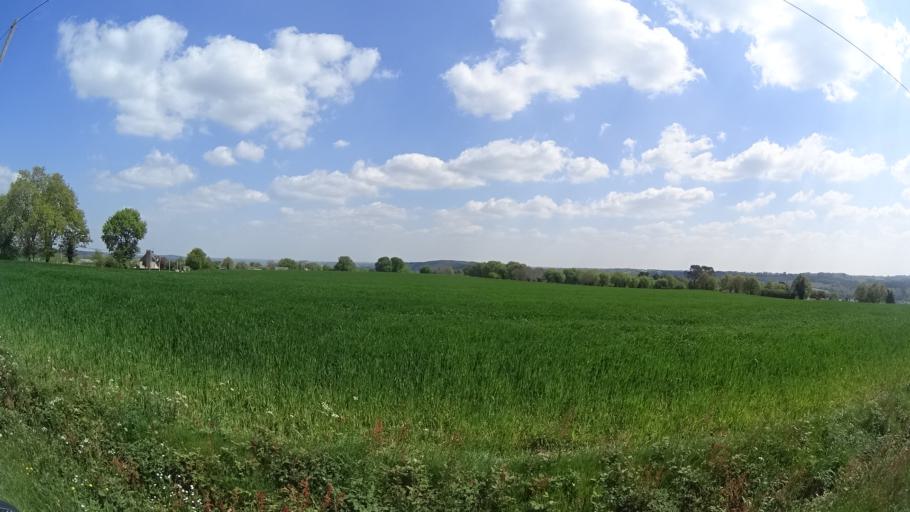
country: FR
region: Brittany
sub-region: Departement du Morbihan
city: Beganne
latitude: 47.5877
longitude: -2.2540
